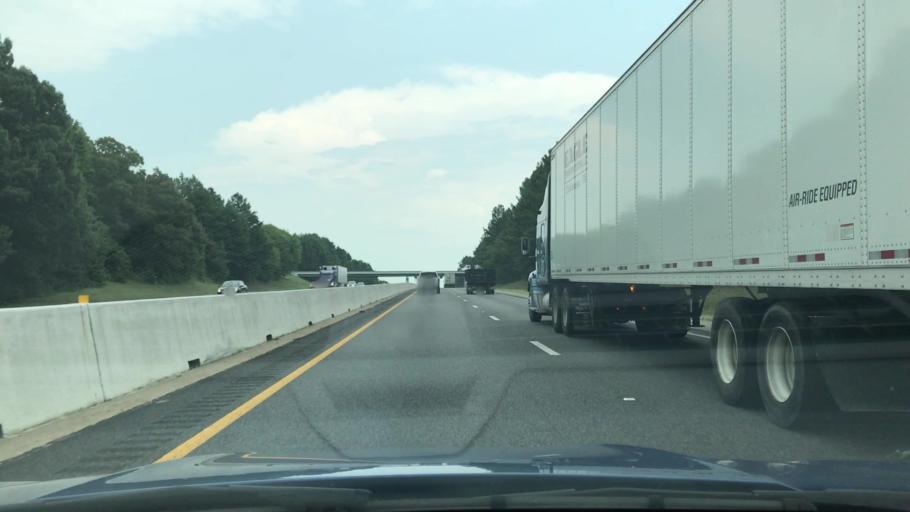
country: US
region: Texas
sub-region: Gregg County
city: Liberty City
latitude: 32.4358
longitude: -94.9744
